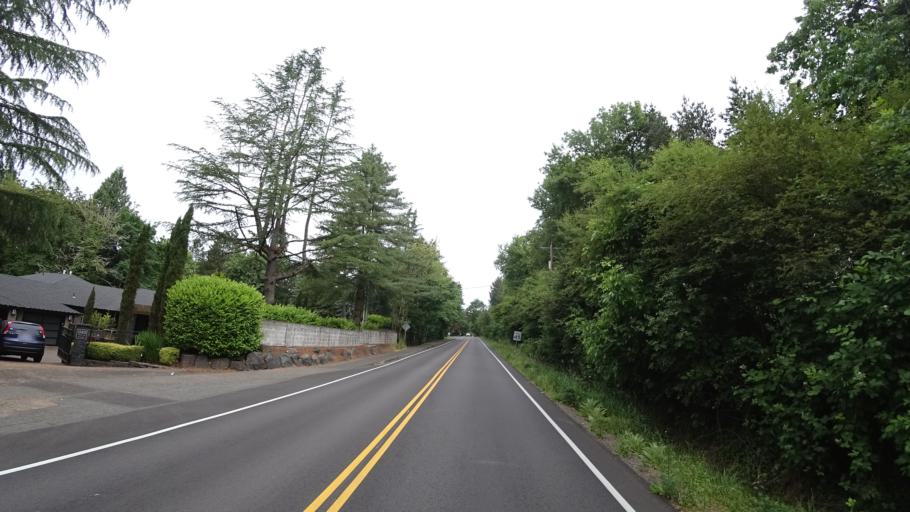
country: US
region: Oregon
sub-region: Clackamas County
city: Lake Oswego
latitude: 45.4347
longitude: -122.6671
